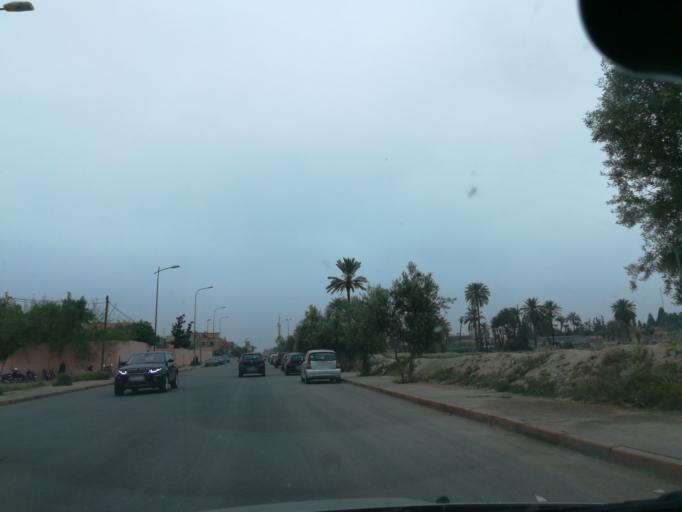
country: MA
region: Marrakech-Tensift-Al Haouz
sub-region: Marrakech
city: Marrakesh
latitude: 31.6690
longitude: -7.9970
